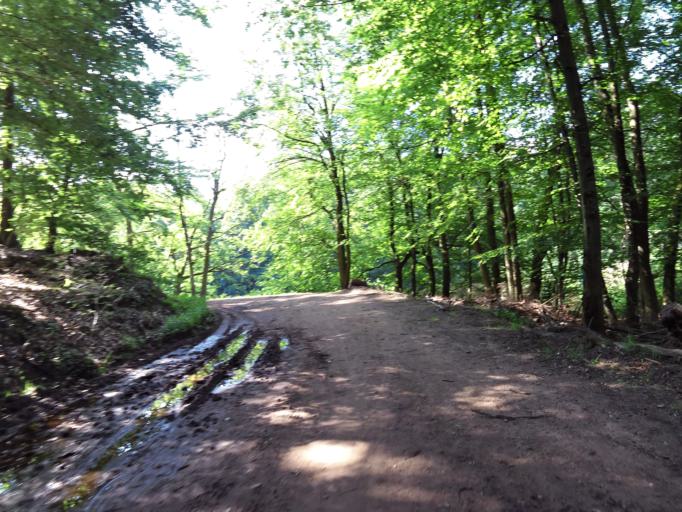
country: DE
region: Rheinland-Pfalz
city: Breunigweiler
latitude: 49.5477
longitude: 7.9609
